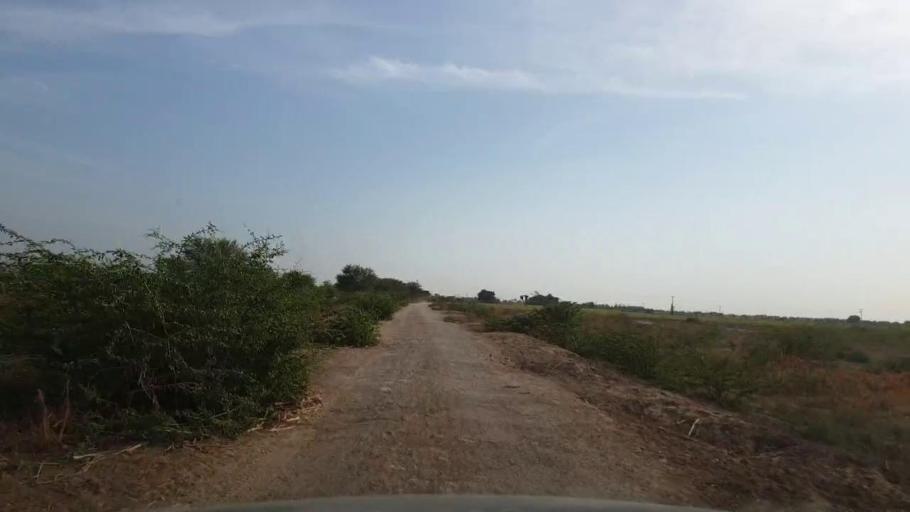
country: PK
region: Sindh
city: Kunri
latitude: 25.1498
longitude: 69.5072
